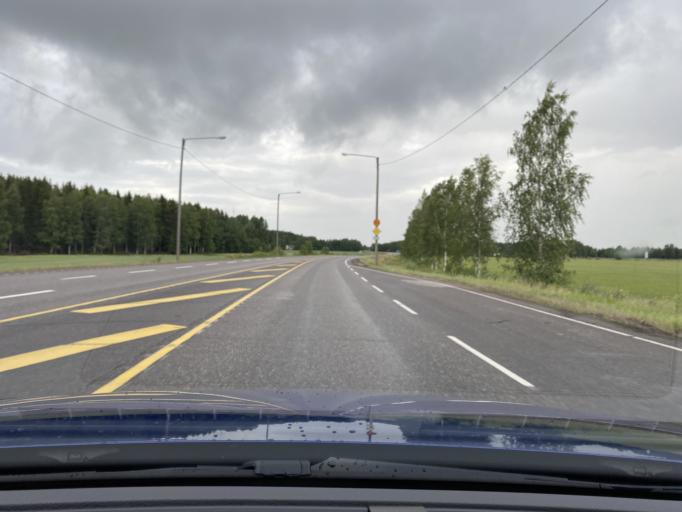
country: FI
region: Uusimaa
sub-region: Helsinki
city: Hyvinge
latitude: 60.5785
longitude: 24.7965
